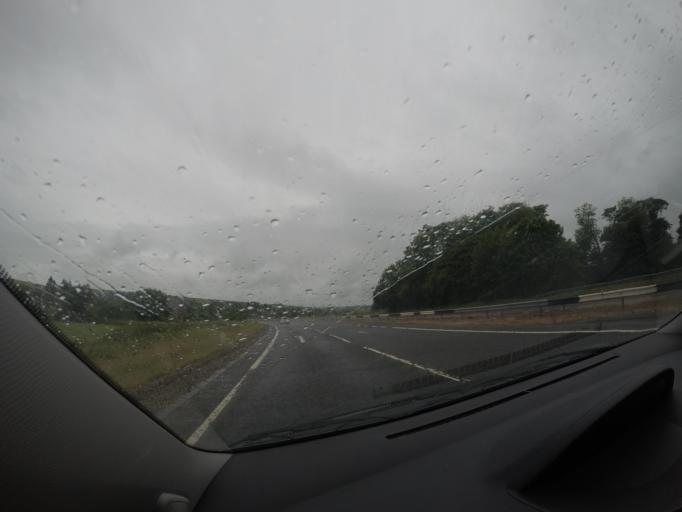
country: GB
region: Scotland
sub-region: Angus
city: Forfar
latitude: 56.7032
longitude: -2.8305
